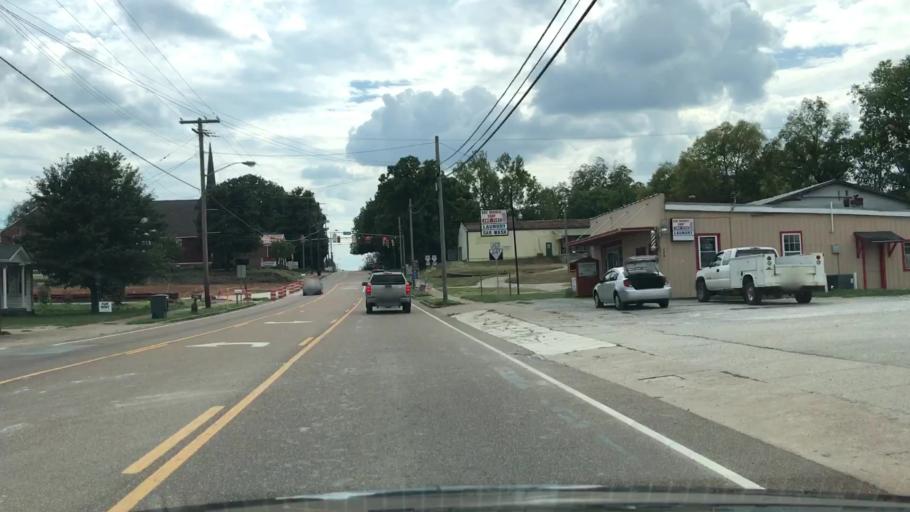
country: US
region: Tennessee
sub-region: Maury County
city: Spring Hill
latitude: 35.7536
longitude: -86.9279
